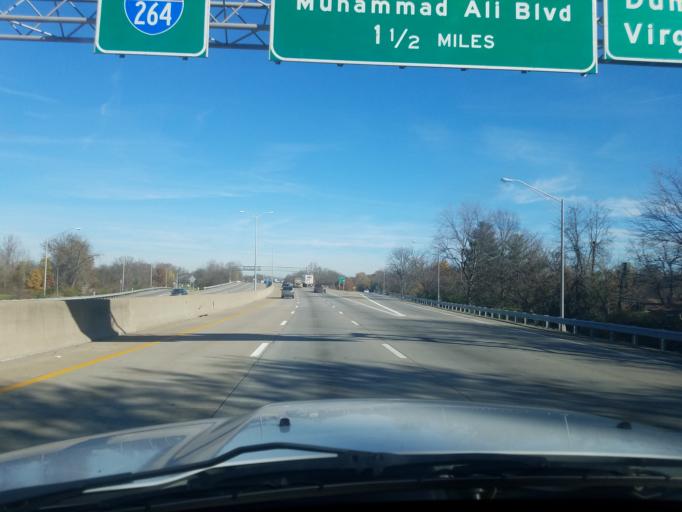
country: US
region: Kentucky
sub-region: Jefferson County
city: Shively
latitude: 38.2356
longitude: -85.8181
